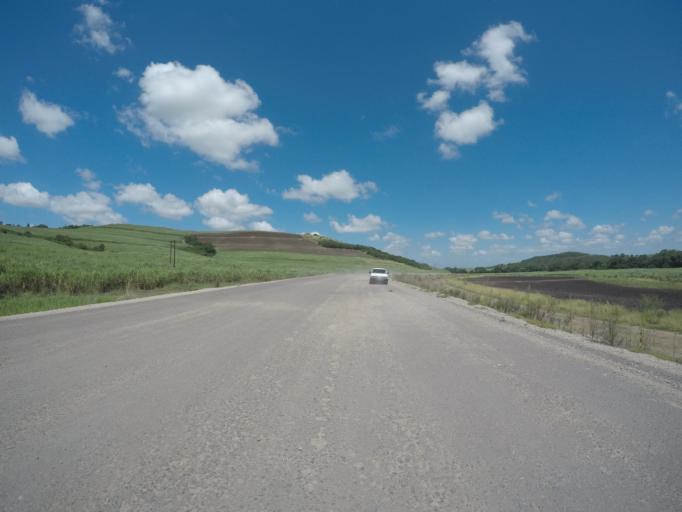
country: ZA
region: KwaZulu-Natal
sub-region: uThungulu District Municipality
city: Empangeni
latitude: -28.6491
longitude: 31.7686
